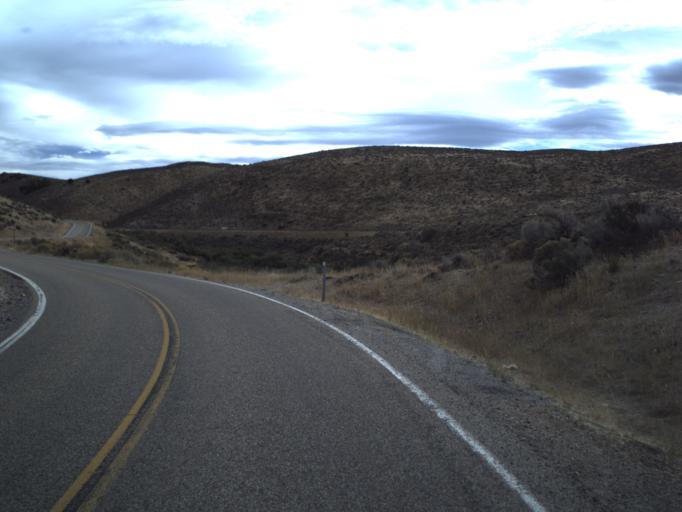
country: US
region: Utah
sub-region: Morgan County
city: Morgan
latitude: 40.9216
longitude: -111.5782
